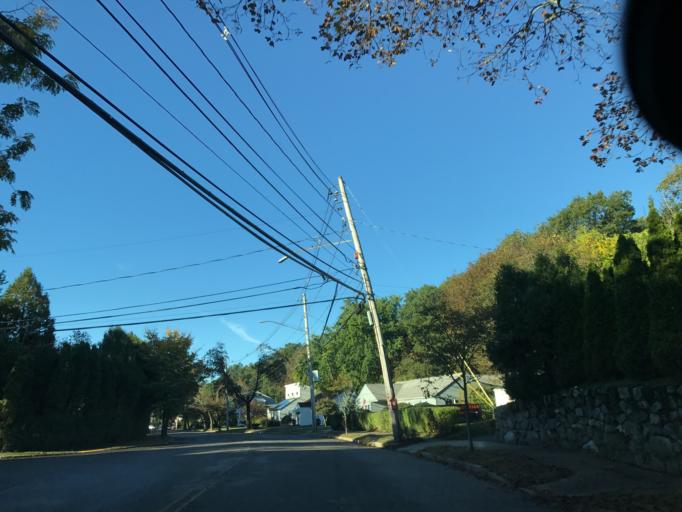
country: US
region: Massachusetts
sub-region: Middlesex County
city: Newton
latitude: 42.2959
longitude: -71.1873
